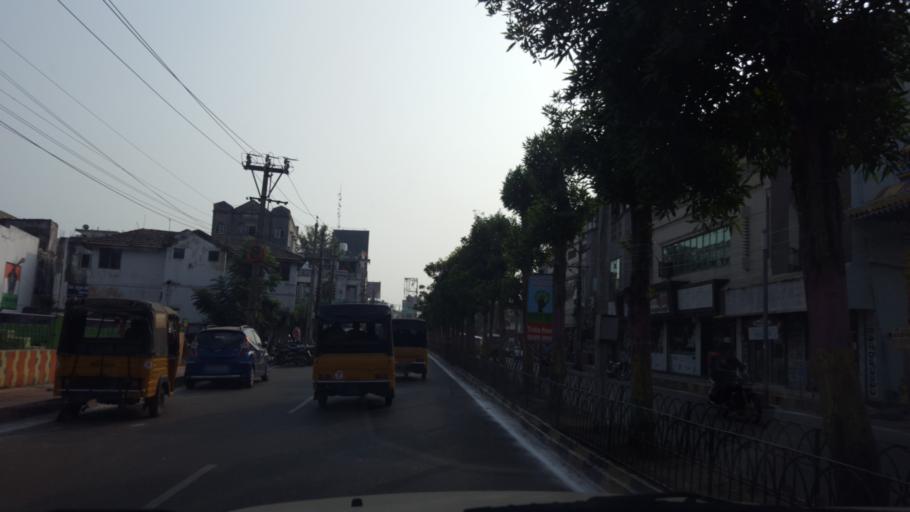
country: IN
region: Andhra Pradesh
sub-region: Srikakulam
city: Srikakulam
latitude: 18.2964
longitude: 83.8946
